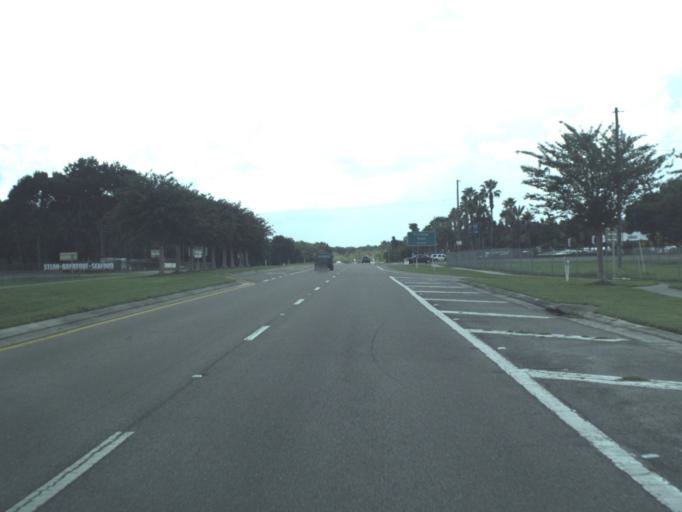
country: US
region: Florida
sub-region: Hillsborough County
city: Plant City
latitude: 28.0378
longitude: -82.1043
